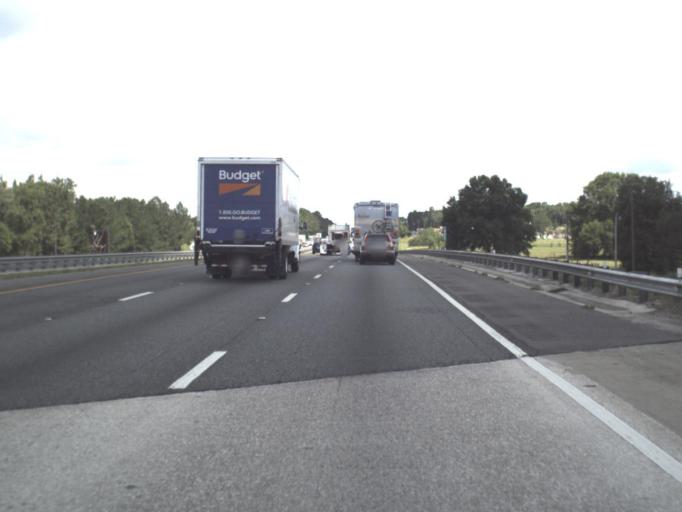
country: US
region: Florida
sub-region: Columbia County
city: Lake City
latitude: 30.1467
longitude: -82.6715
